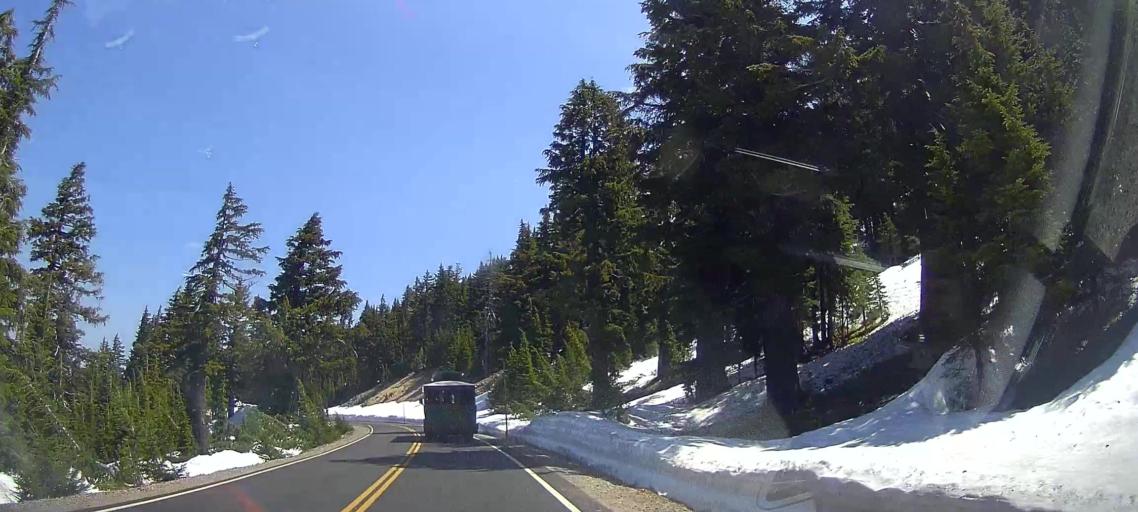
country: US
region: Oregon
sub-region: Jackson County
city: Shady Cove
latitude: 42.9728
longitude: -122.1448
